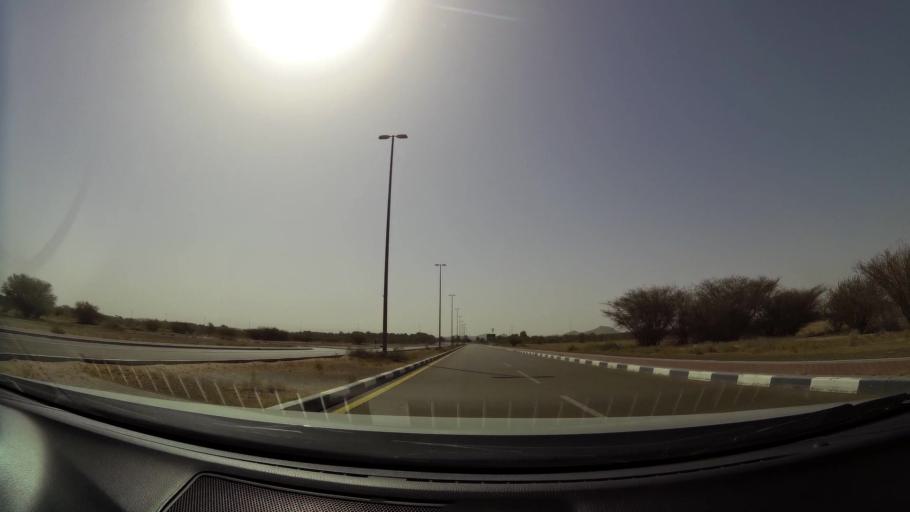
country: OM
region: Al Buraimi
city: Al Buraymi
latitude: 24.3167
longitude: 55.7923
